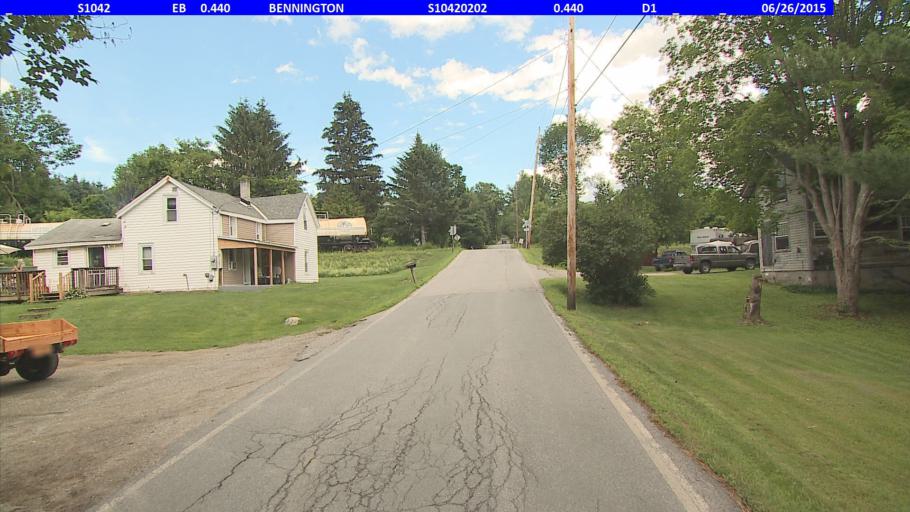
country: US
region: Vermont
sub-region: Bennington County
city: North Bennington
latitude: 42.9147
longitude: -73.2195
